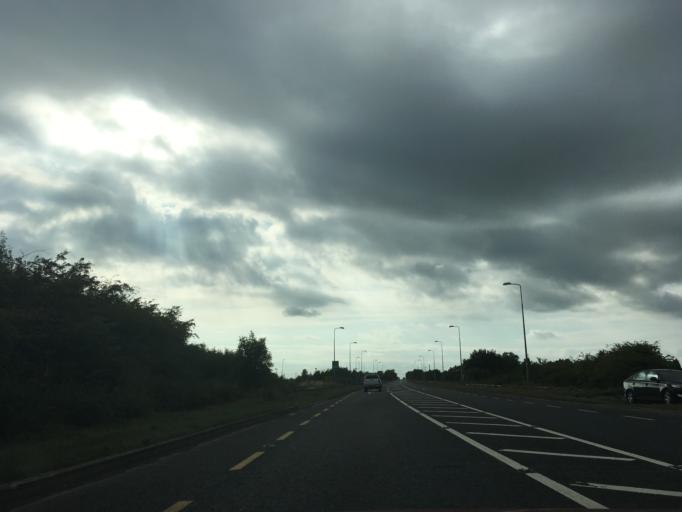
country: IE
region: Leinster
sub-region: Loch Garman
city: Loch Garman
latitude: 52.3393
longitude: -6.5613
